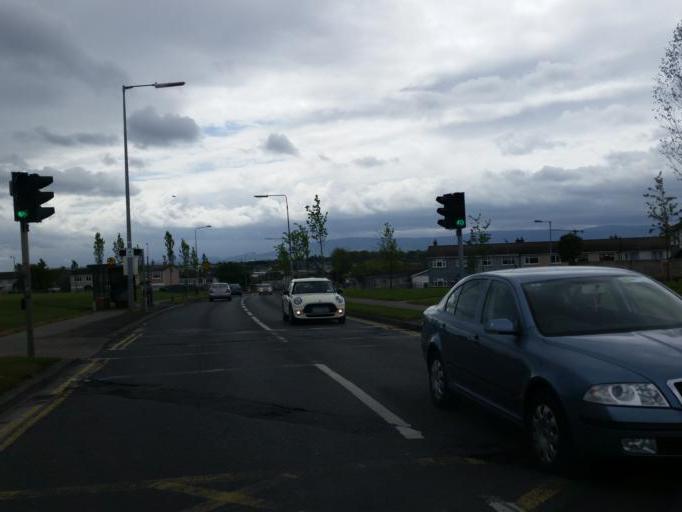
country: IE
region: Leinster
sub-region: Dublin City
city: Finglas
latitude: 53.3838
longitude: -6.3121
